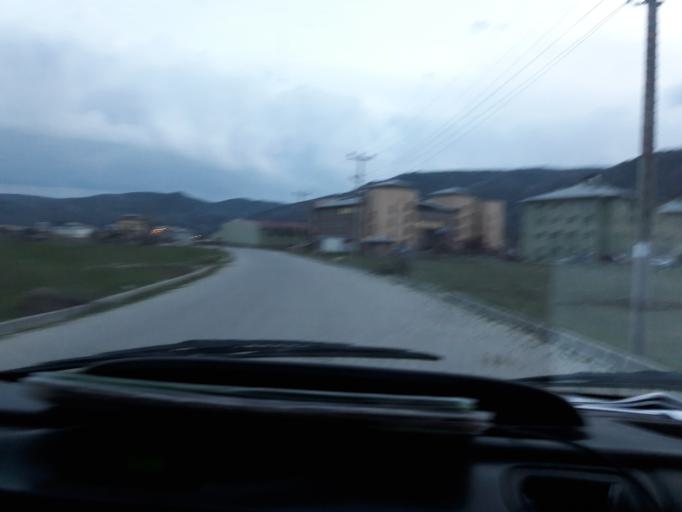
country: TR
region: Giresun
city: Alucra
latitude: 40.3250
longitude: 38.7712
